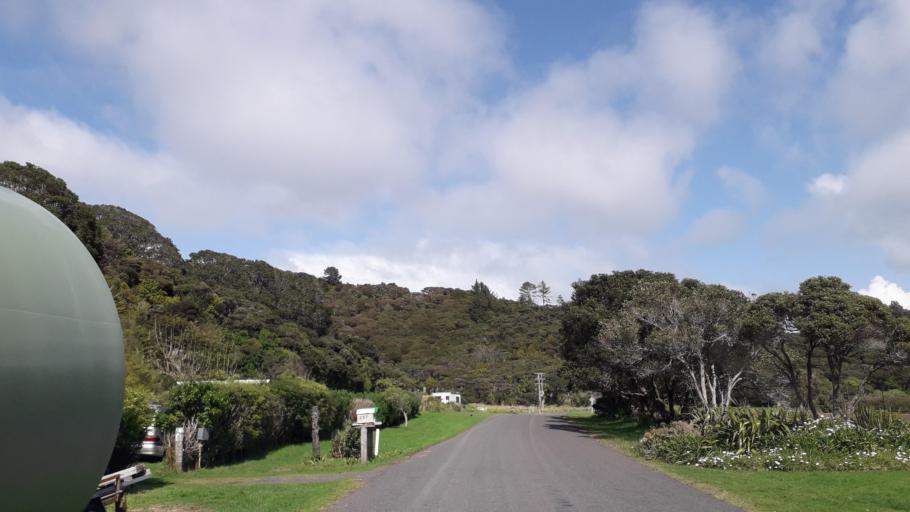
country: NZ
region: Northland
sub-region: Far North District
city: Paihia
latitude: -35.2367
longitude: 174.2599
